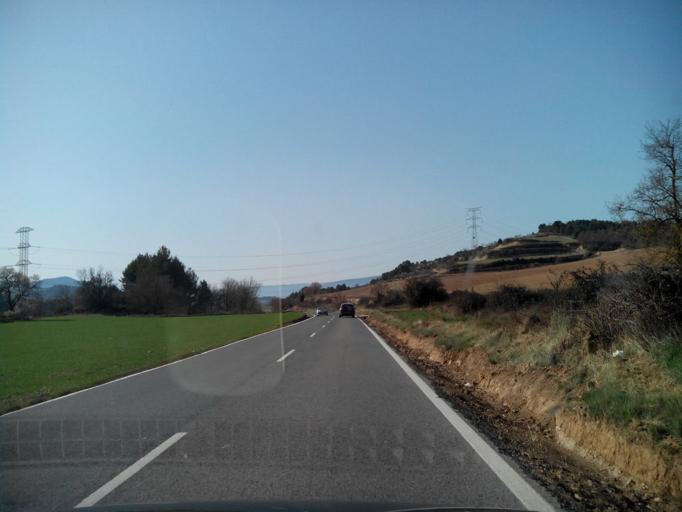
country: ES
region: Catalonia
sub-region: Provincia de Tarragona
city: Fores
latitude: 41.4667
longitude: 1.2715
